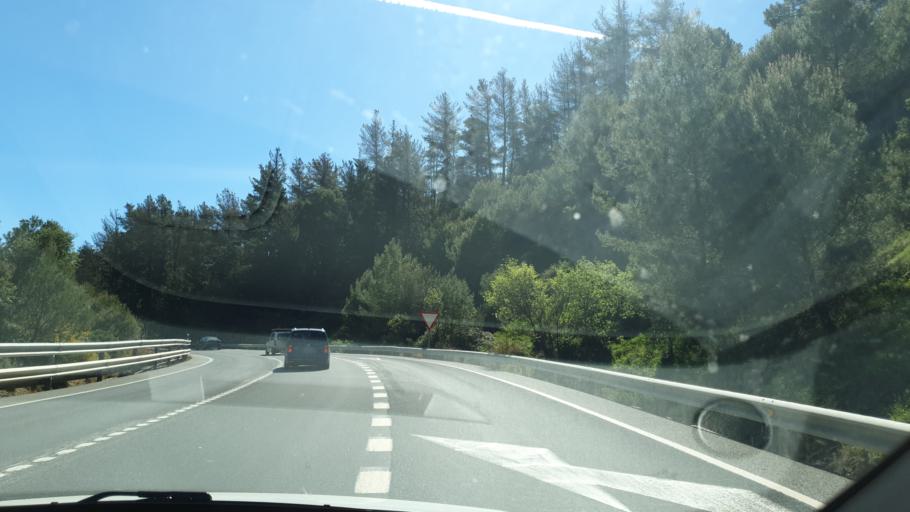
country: ES
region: Andalusia
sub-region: Provincia de Malaga
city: Ojen
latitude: 36.5741
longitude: -4.8600
